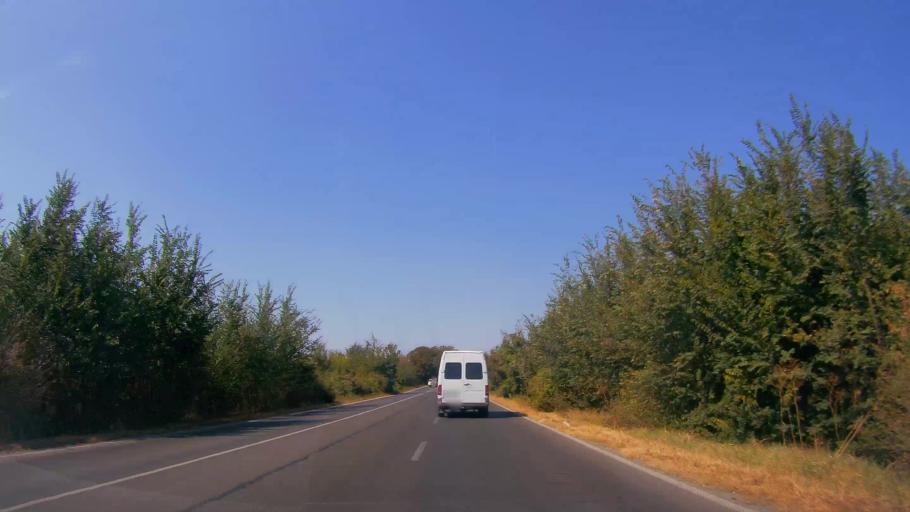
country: BG
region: Razgrad
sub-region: Obshtina Tsar Kaloyan
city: Tsar Kaloyan
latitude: 43.6302
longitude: 26.2039
